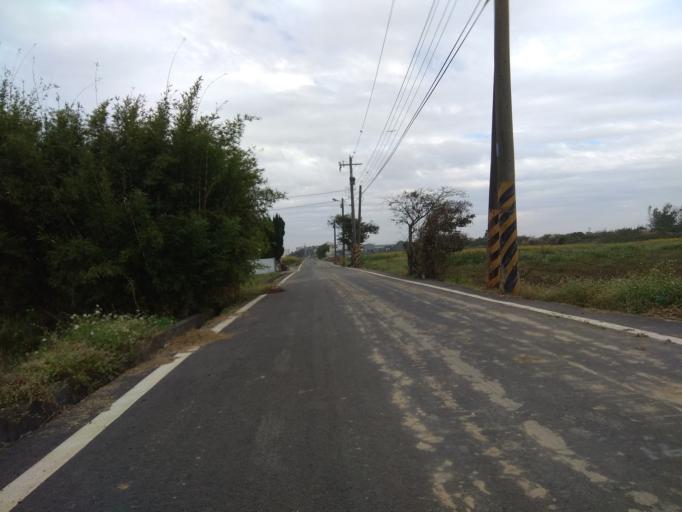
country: TW
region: Taiwan
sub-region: Hsinchu
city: Zhubei
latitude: 24.9847
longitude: 121.0476
